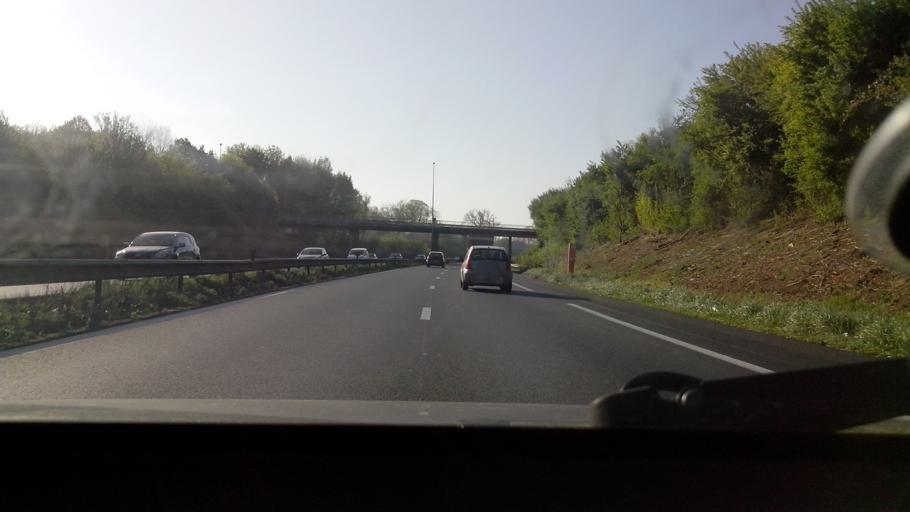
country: FR
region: Ile-de-France
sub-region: Departement de Seine-et-Marne
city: Brie-Comte-Robert
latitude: 48.6792
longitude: 2.6075
